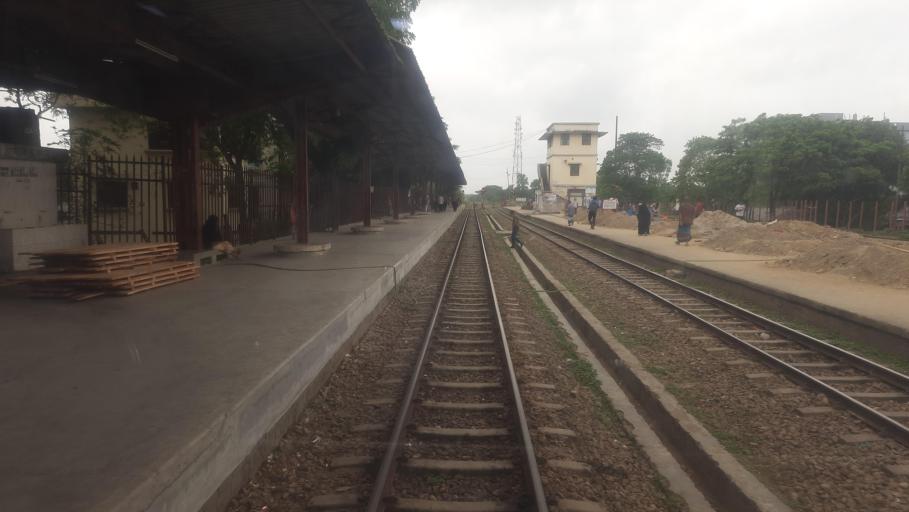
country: BD
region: Dhaka
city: Bhairab Bazar
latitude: 24.0503
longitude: 90.9775
